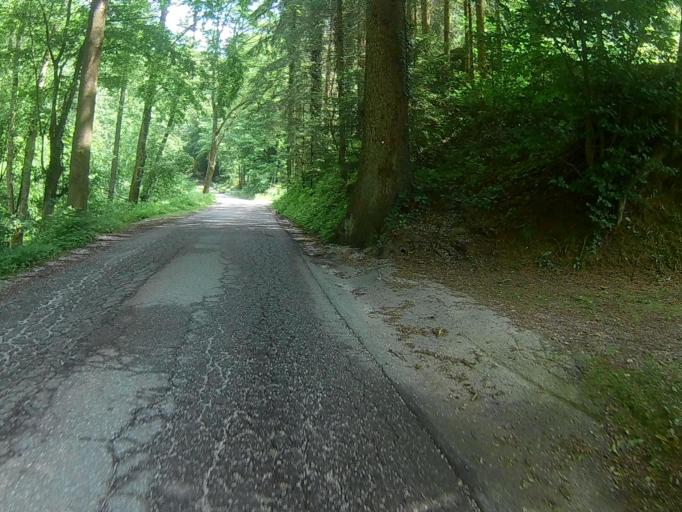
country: SI
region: Maribor
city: Kamnica
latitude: 46.5941
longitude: 15.5941
